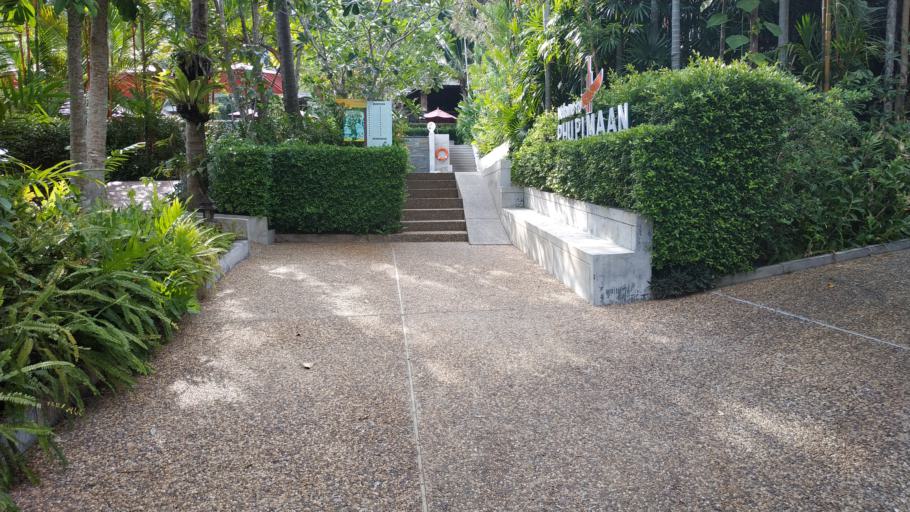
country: TH
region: Phangnga
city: Ban Ao Nang
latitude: 8.0370
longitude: 98.8313
